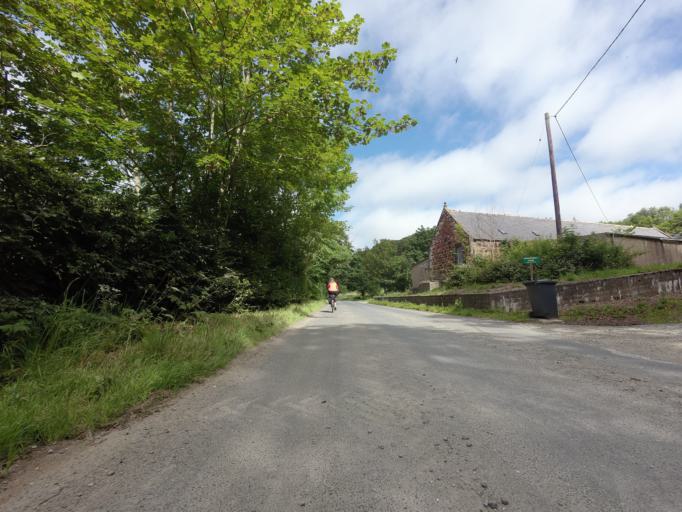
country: GB
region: Scotland
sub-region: Aberdeenshire
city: Turriff
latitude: 57.5482
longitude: -2.4826
